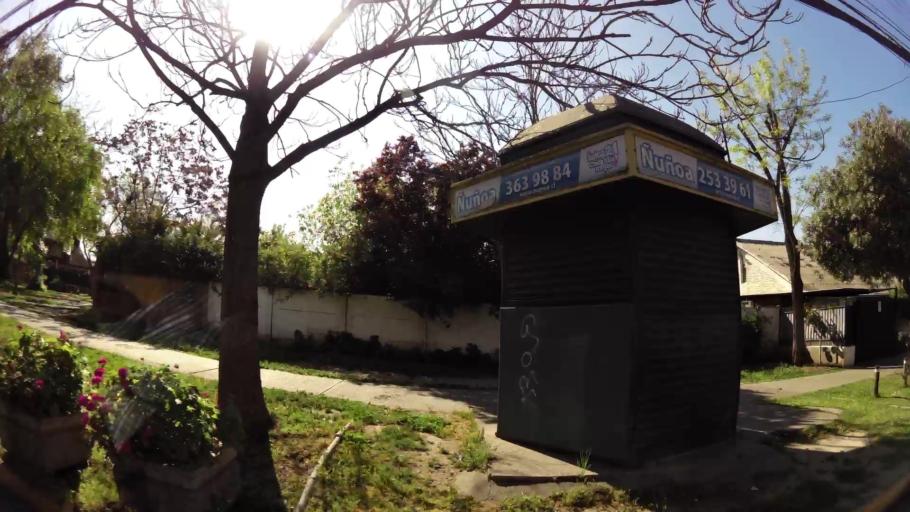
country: CL
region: Santiago Metropolitan
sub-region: Provincia de Santiago
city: Villa Presidente Frei, Nunoa, Santiago, Chile
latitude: -33.4405
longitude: -70.5778
